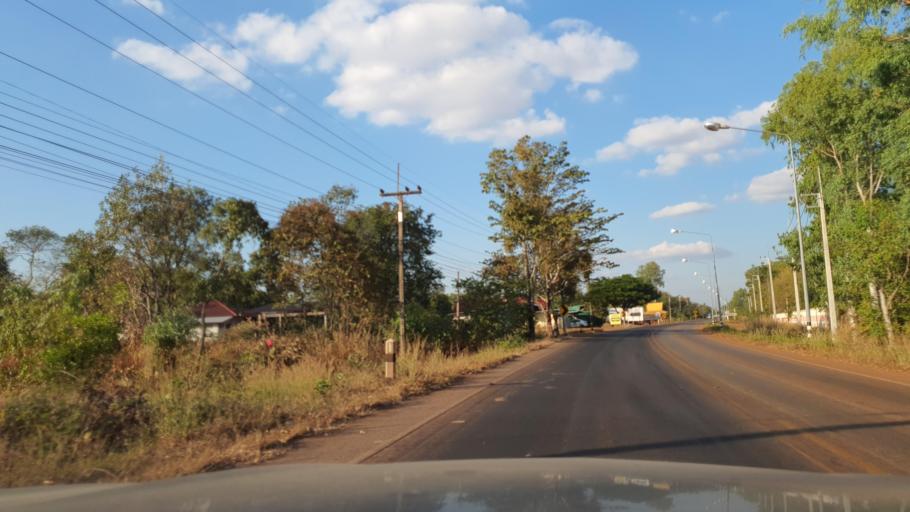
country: TH
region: Sakon Nakhon
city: Phon Na Kaeo
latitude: 17.2697
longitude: 104.1915
